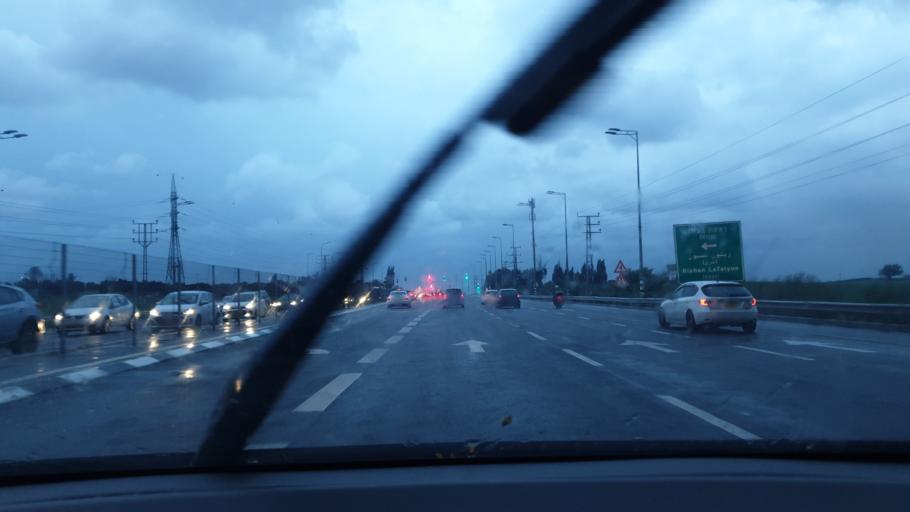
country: IL
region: Central District
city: Kefar Habad
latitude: 31.9720
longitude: 34.8417
